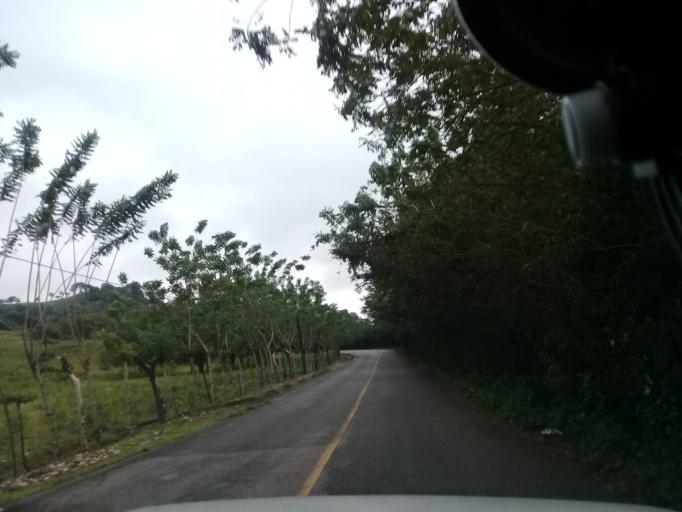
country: MX
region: Veracruz
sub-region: Chalma
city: San Pedro Coyutla
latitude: 21.2165
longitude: -98.4291
